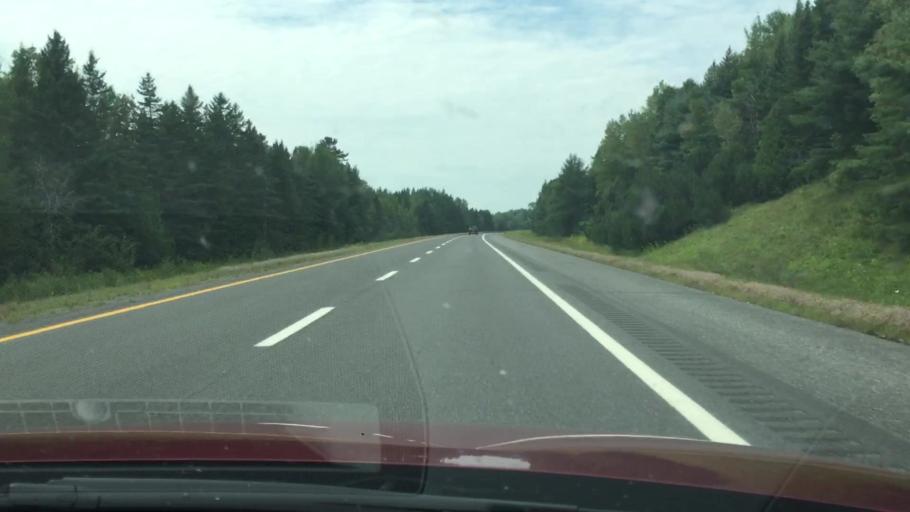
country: US
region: Maine
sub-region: Aroostook County
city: Houlton
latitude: 46.1373
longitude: -67.9017
